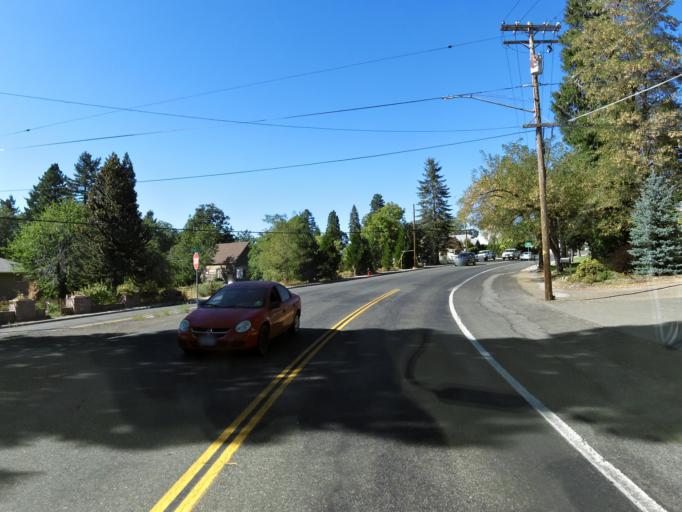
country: US
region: California
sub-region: Siskiyou County
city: Mount Shasta
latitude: 41.3061
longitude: -122.3108
